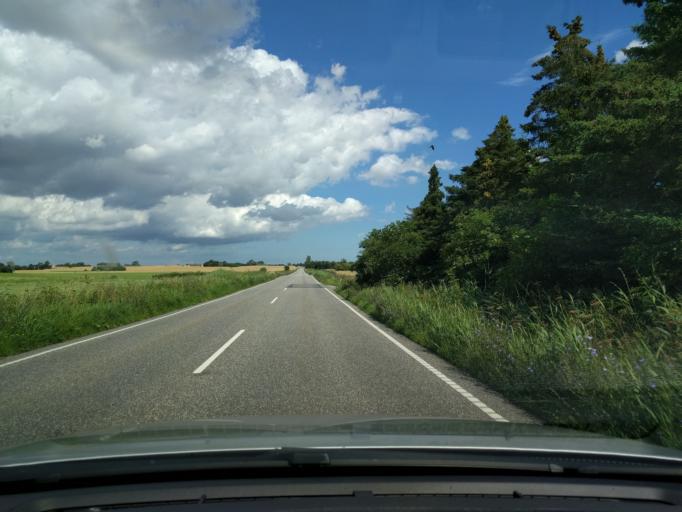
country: DK
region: Zealand
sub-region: Guldborgsund Kommune
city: Stubbekobing
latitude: 54.9067
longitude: 12.1254
